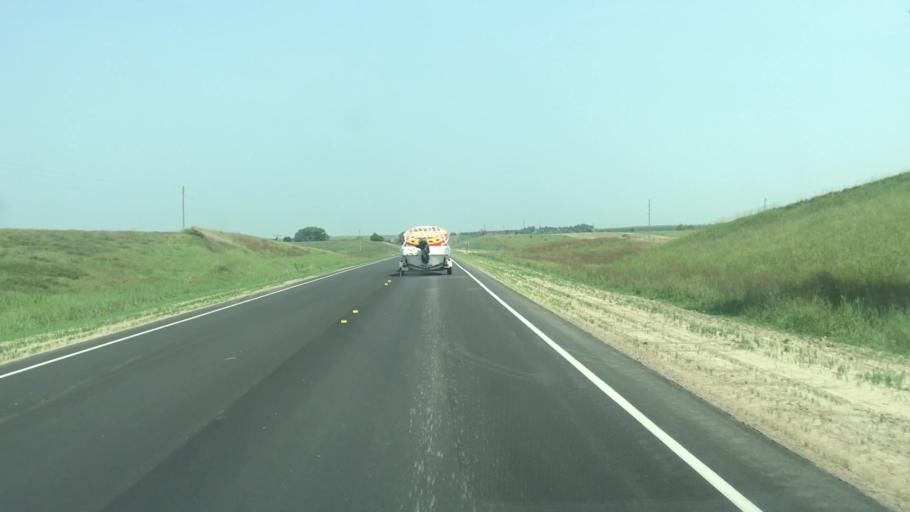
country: US
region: Nebraska
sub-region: Sherman County
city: Loup City
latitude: 41.2632
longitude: -98.9278
